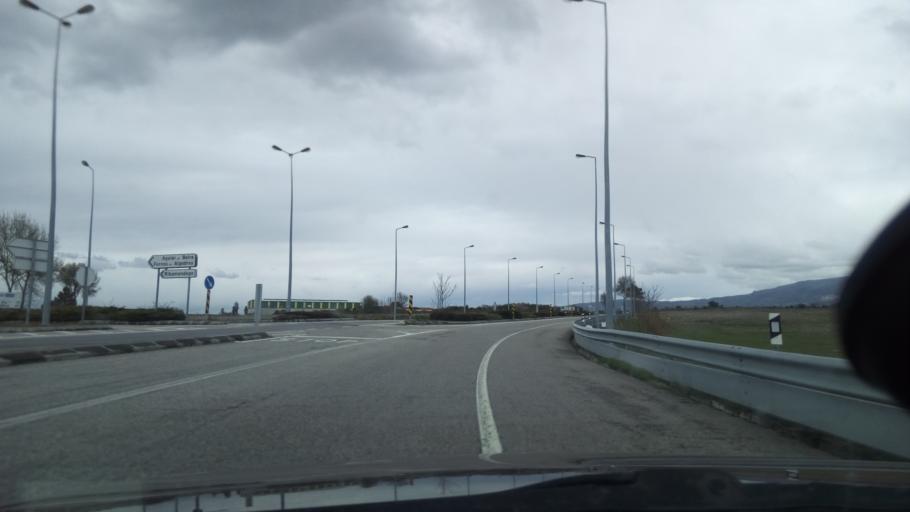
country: PT
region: Guarda
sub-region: Fornos de Algodres
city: Fornos de Algodres
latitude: 40.5346
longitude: -7.5721
